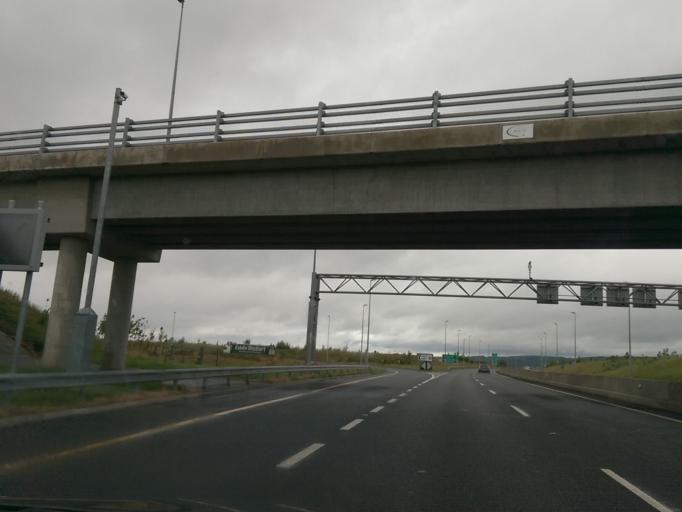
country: IE
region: Munster
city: Moyross
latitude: 52.6603
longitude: -8.6934
